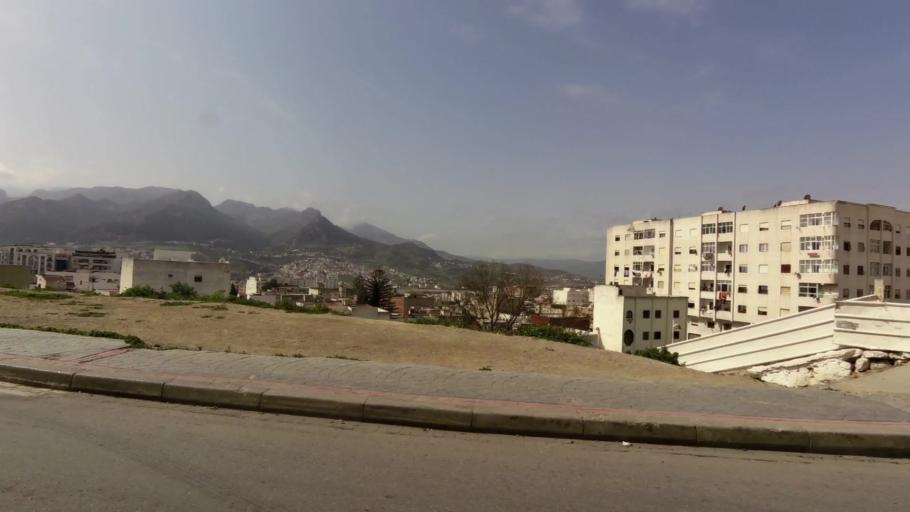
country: MA
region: Tanger-Tetouan
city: Tetouan
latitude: 35.5758
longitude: -5.3796
